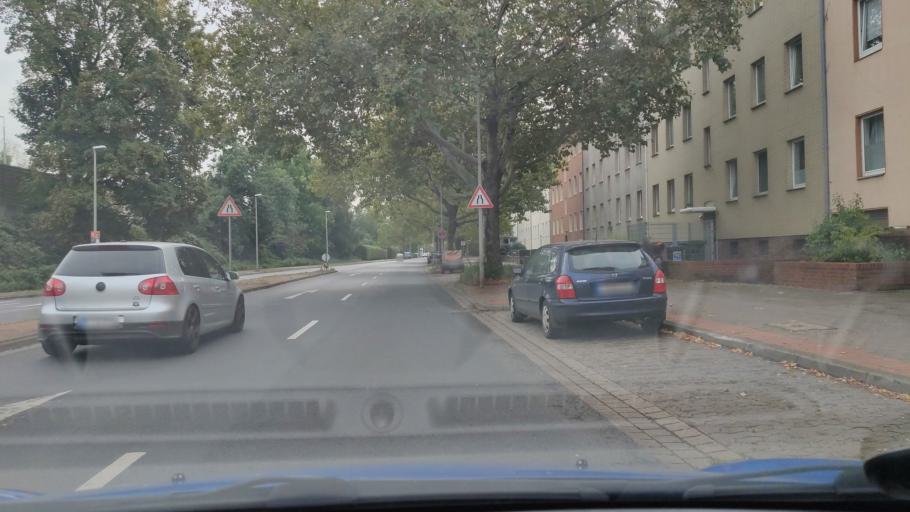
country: DE
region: Lower Saxony
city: Ronnenberg
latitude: 52.3568
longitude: 9.6767
